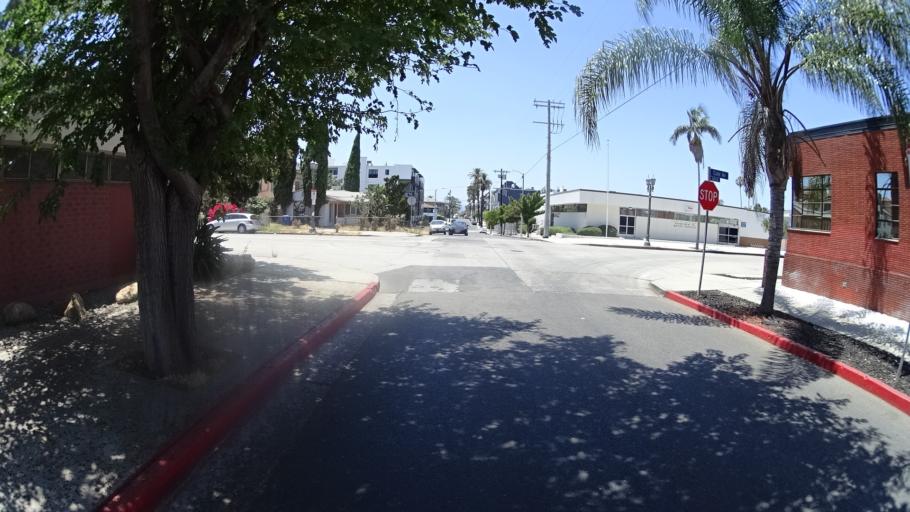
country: US
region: California
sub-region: Los Angeles County
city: Hollywood
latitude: 34.0853
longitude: -118.3297
